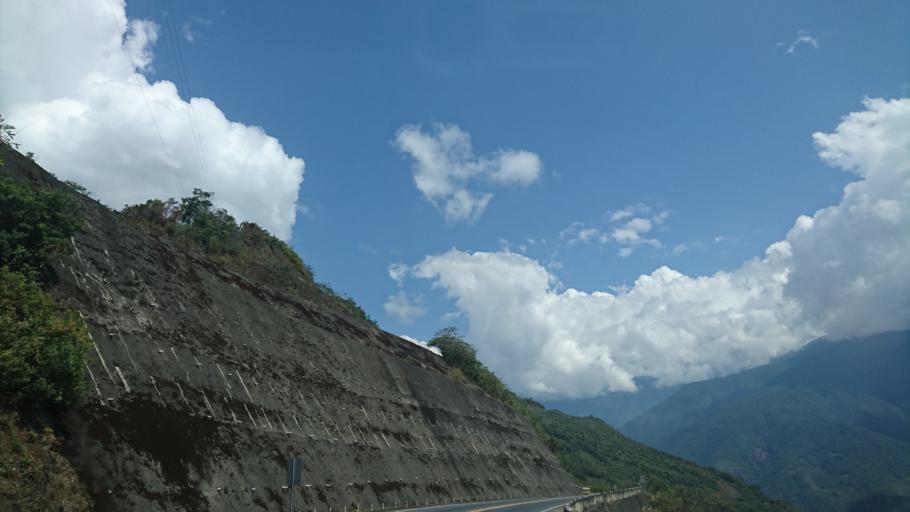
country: BO
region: La Paz
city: Coroico
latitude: -16.2138
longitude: -67.7904
